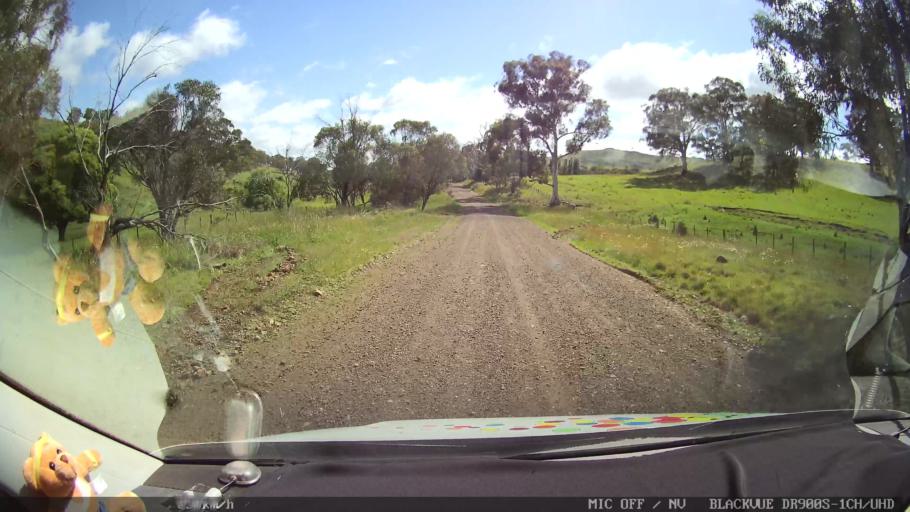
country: AU
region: New South Wales
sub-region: Guyra
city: Guyra
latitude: -29.9876
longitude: 151.6907
